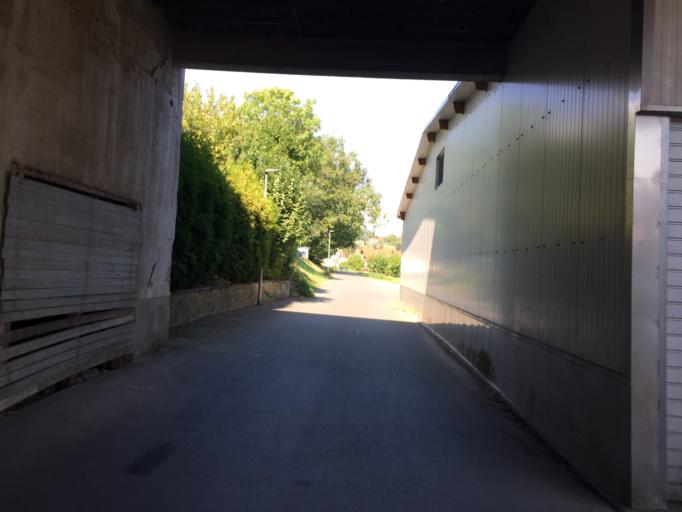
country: DE
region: Hesse
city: Laufdorf
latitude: 50.4967
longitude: 8.4263
